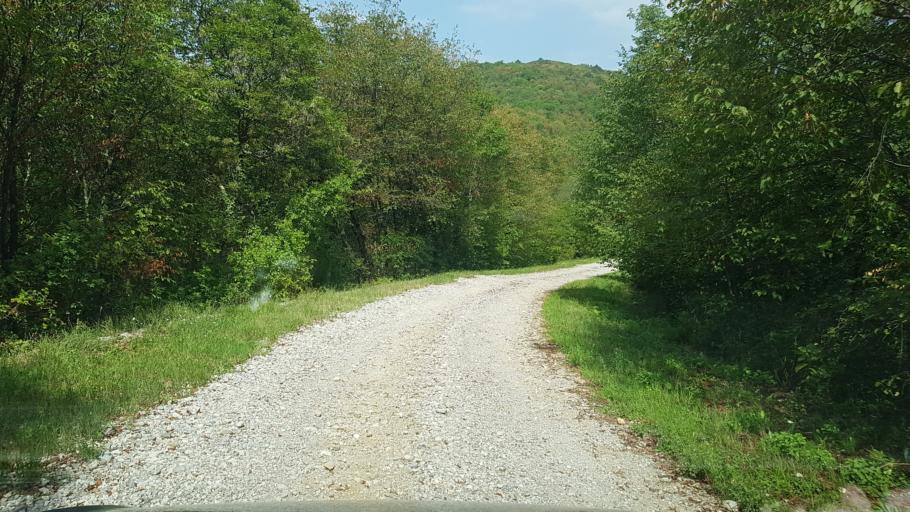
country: SI
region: Nova Gorica
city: Solkan
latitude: 46.0073
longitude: 13.6442
